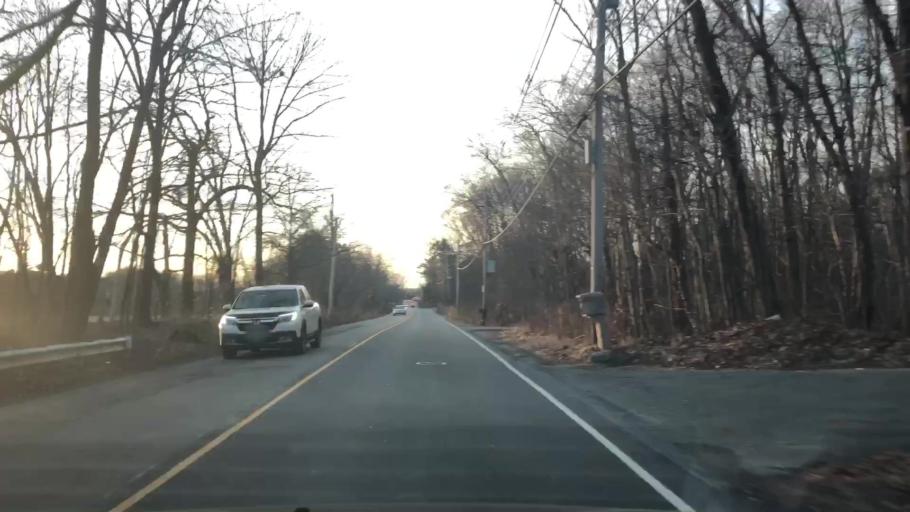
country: US
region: Massachusetts
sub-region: Essex County
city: North Andover
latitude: 42.7147
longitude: -71.1094
